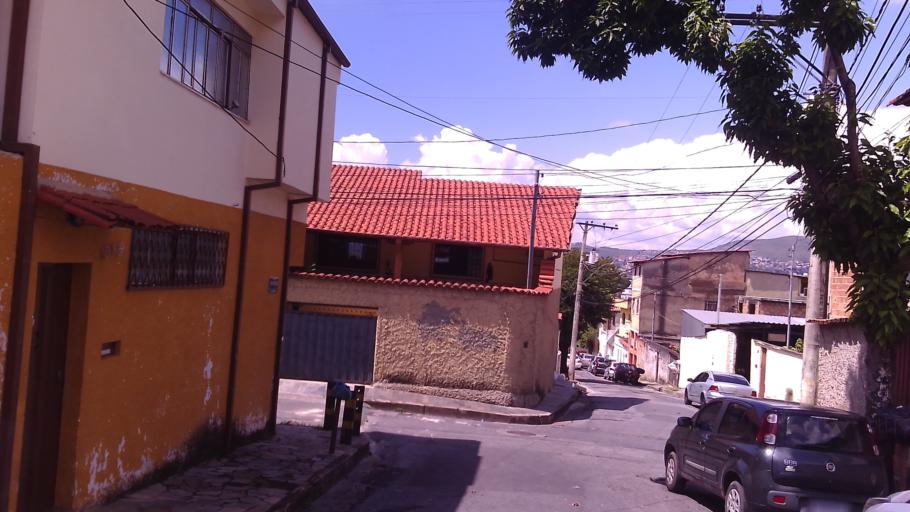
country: BR
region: Minas Gerais
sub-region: Belo Horizonte
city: Belo Horizonte
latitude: -19.8999
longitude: -43.9150
